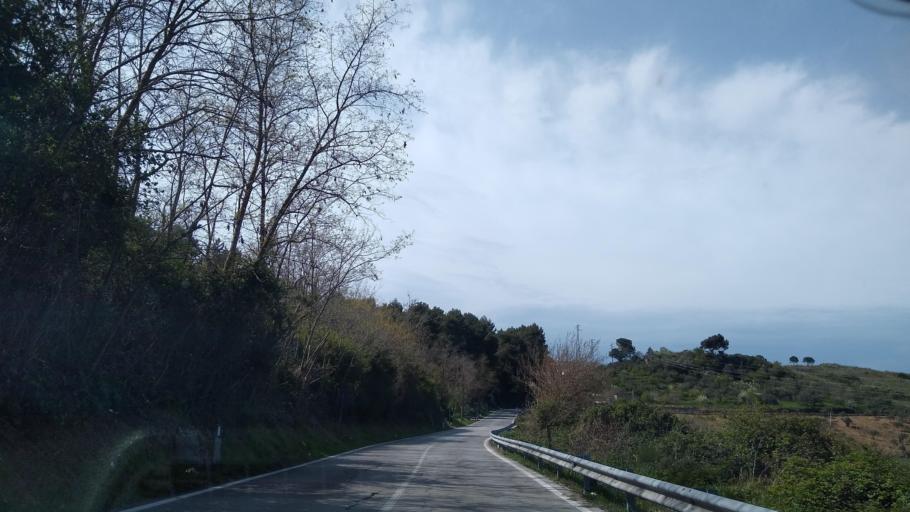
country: IT
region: Sicily
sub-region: Palermo
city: Pioppo
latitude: 38.0396
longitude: 13.2037
